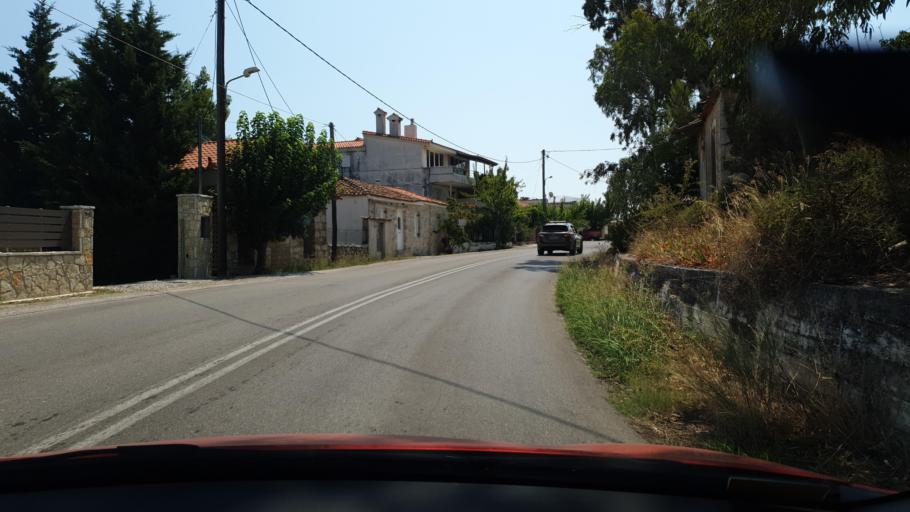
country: GR
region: Central Greece
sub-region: Nomos Evvoias
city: Aliveri
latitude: 38.4647
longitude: 24.1176
